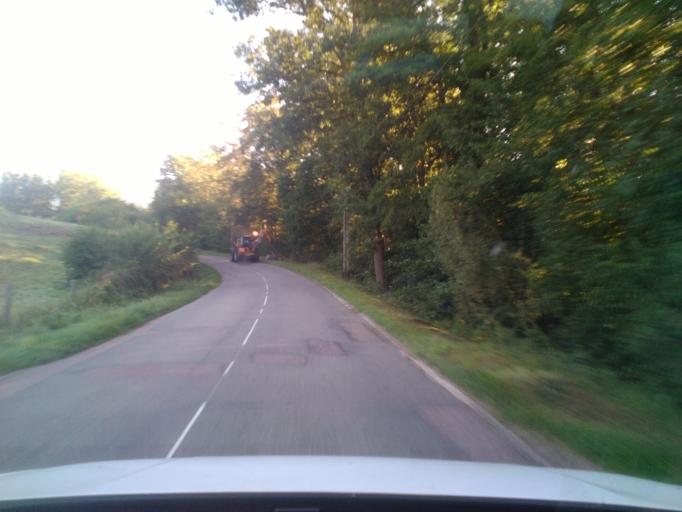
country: FR
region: Lorraine
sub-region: Departement des Vosges
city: Saint-Die-des-Vosges
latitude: 48.3012
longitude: 6.9518
